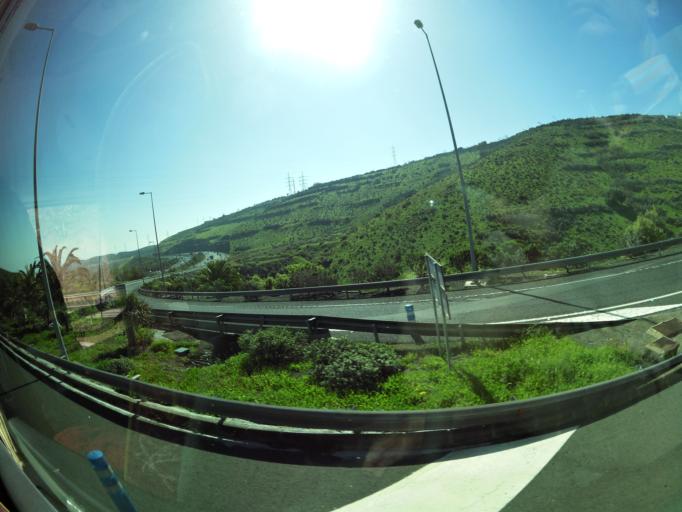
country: ES
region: Canary Islands
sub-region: Provincia de Las Palmas
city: Las Palmas de Gran Canaria
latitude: 28.0567
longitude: -15.4422
